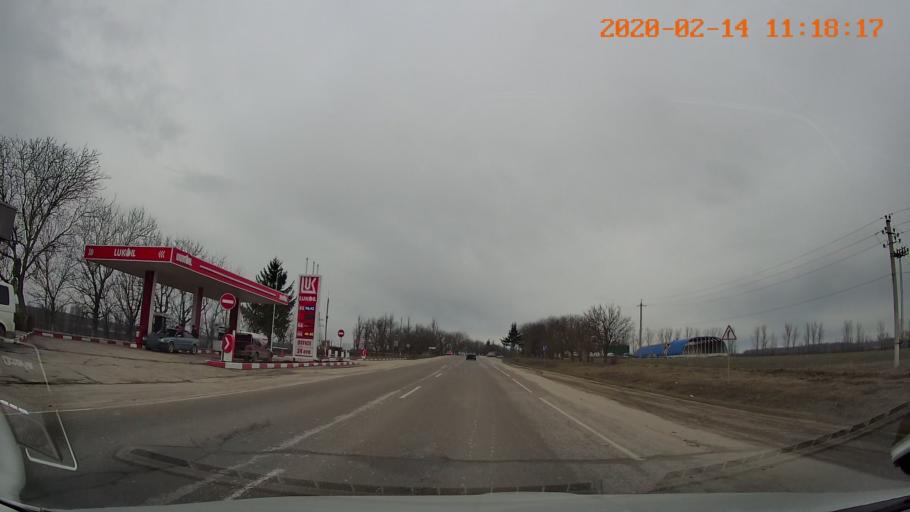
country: MD
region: Briceni
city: Briceni
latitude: 48.2649
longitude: 27.1777
